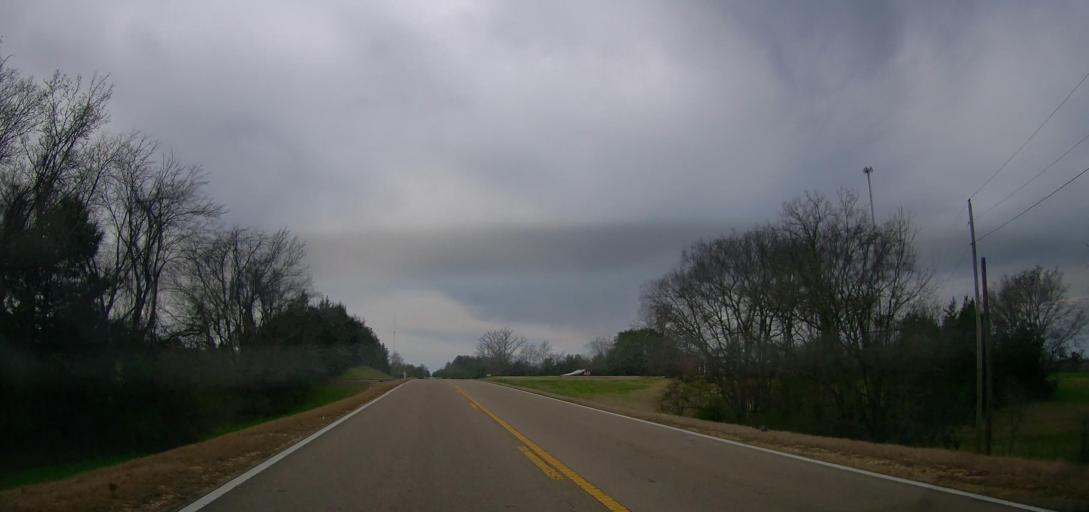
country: US
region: Mississippi
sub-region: Itawamba County
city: Mantachie
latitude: 34.2604
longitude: -88.5203
